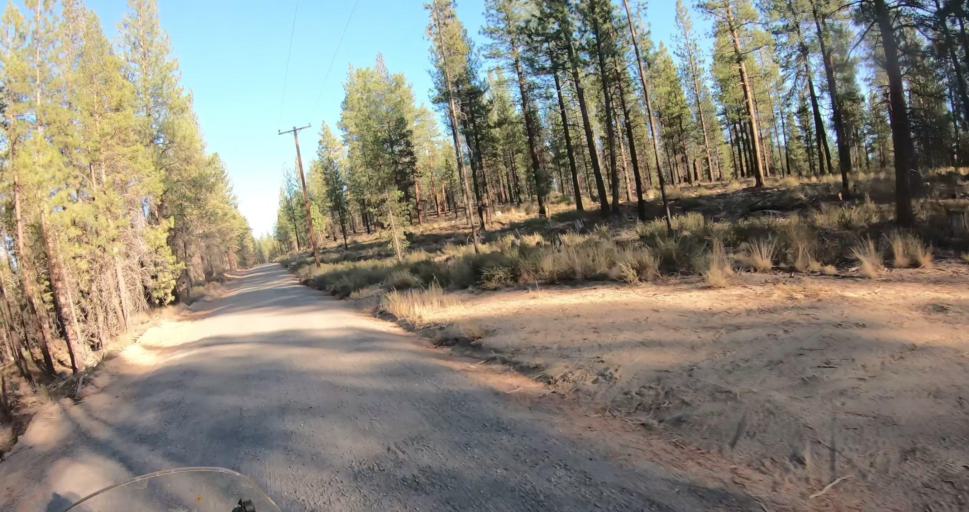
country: US
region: Oregon
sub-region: Deschutes County
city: La Pine
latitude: 43.7253
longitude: -121.4116
